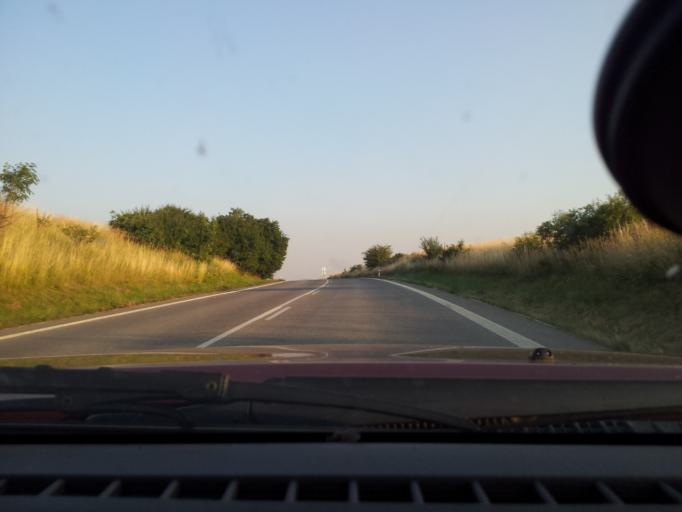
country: SK
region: Trnavsky
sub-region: Okres Senica
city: Senica
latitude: 48.7296
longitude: 17.3563
